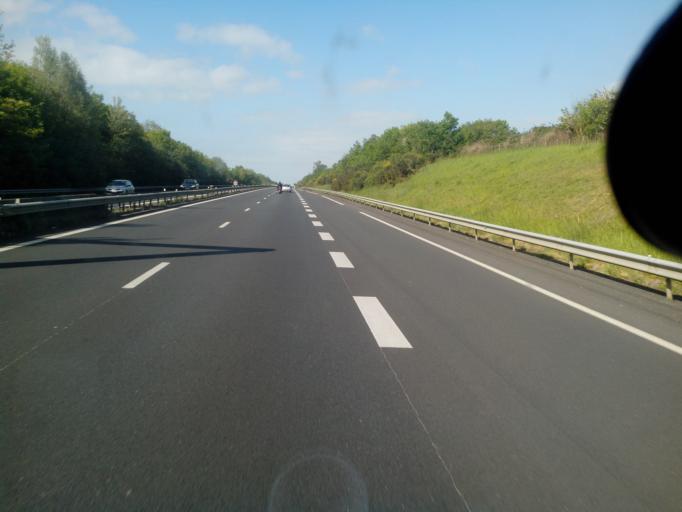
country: FR
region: Lower Normandy
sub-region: Departement du Calvados
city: Troarn
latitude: 49.1821
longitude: -0.1981
